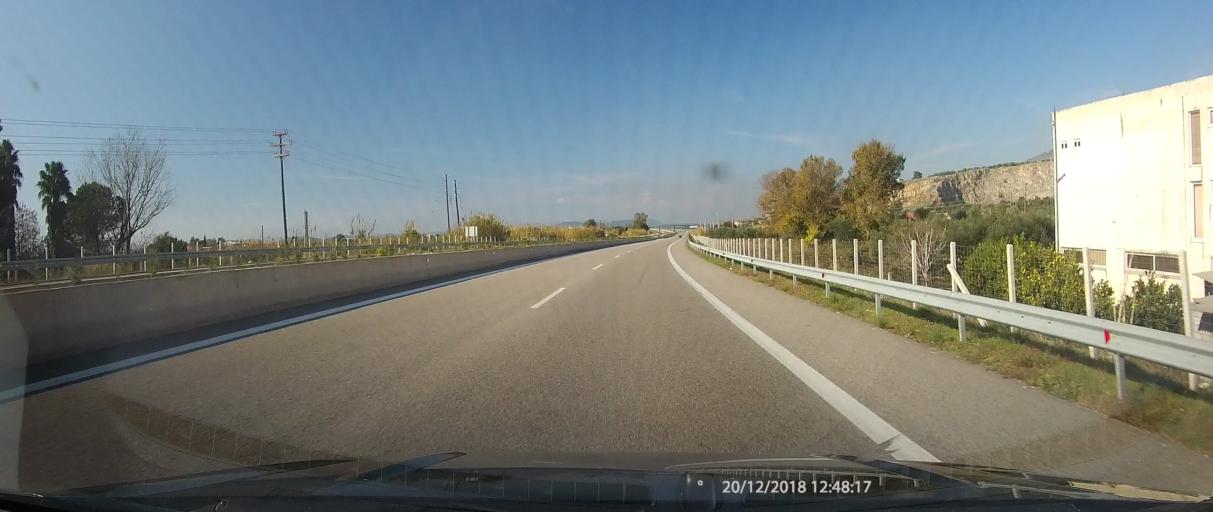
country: GR
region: West Greece
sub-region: Nomos Aitolias kai Akarnanias
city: Mesolongi
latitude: 38.3945
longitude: 21.4230
